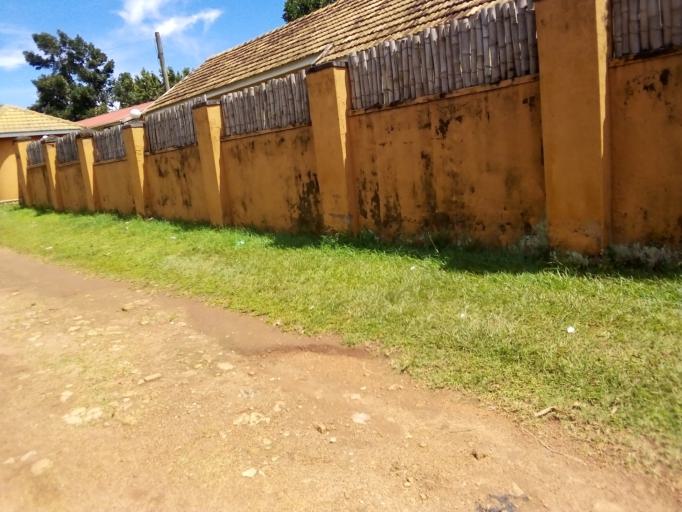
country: UG
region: Central Region
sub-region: Wakiso District
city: Entebbe
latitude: 0.0524
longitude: 32.4634
